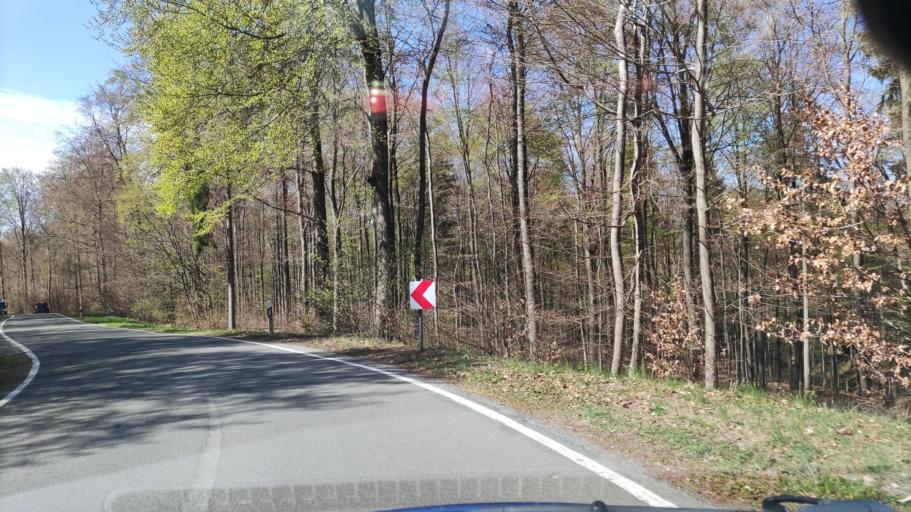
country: DE
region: Lower Saxony
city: Eimen
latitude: 51.8980
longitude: 9.8183
